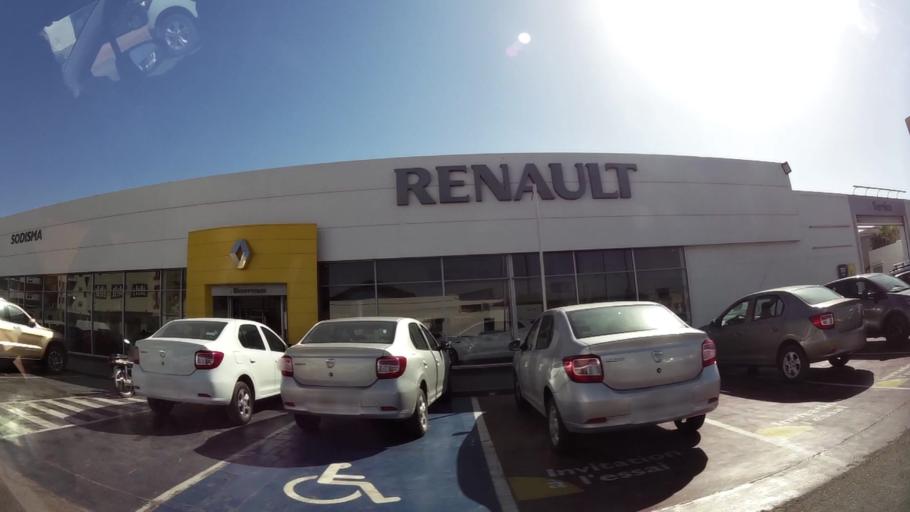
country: MA
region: Souss-Massa-Draa
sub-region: Agadir-Ida-ou-Tnan
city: Agadir
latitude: 30.4194
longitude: -9.5789
